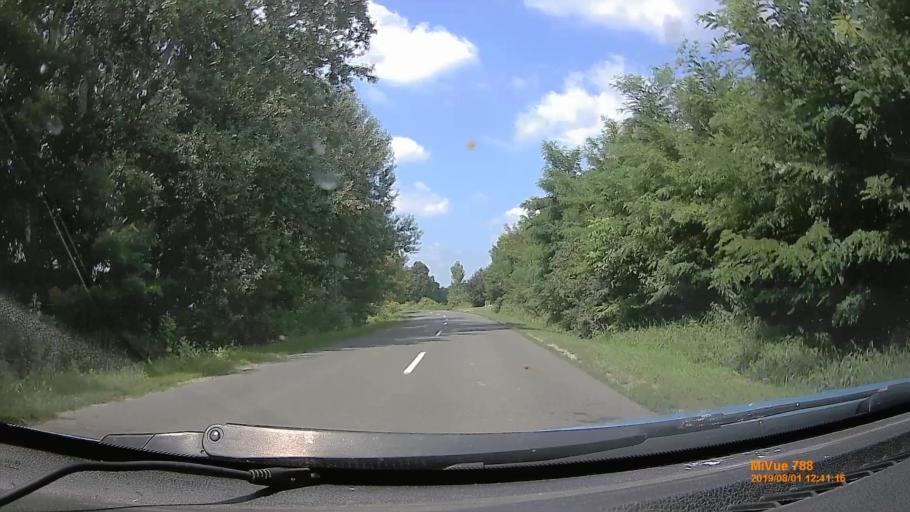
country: HU
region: Baranya
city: Harkany
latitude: 45.8358
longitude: 18.1774
